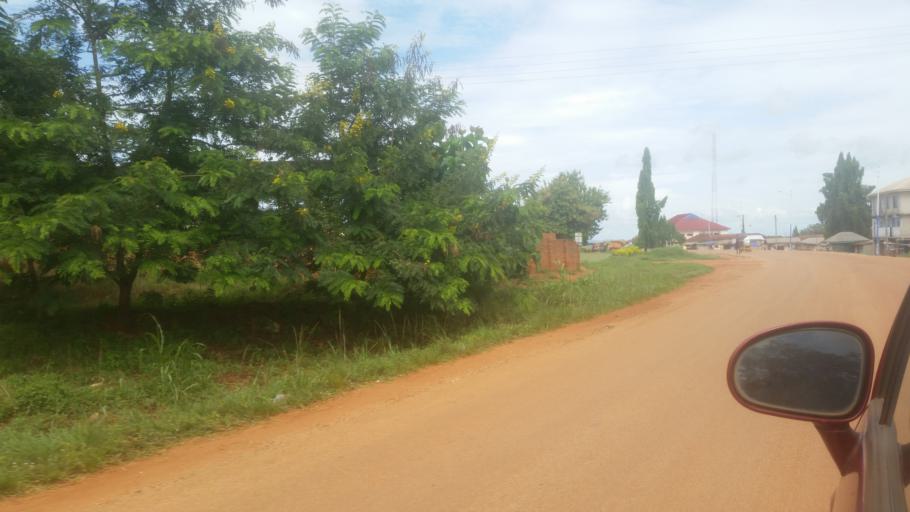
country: GH
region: Western
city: Bibiani
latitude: 6.8055
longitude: -2.5228
